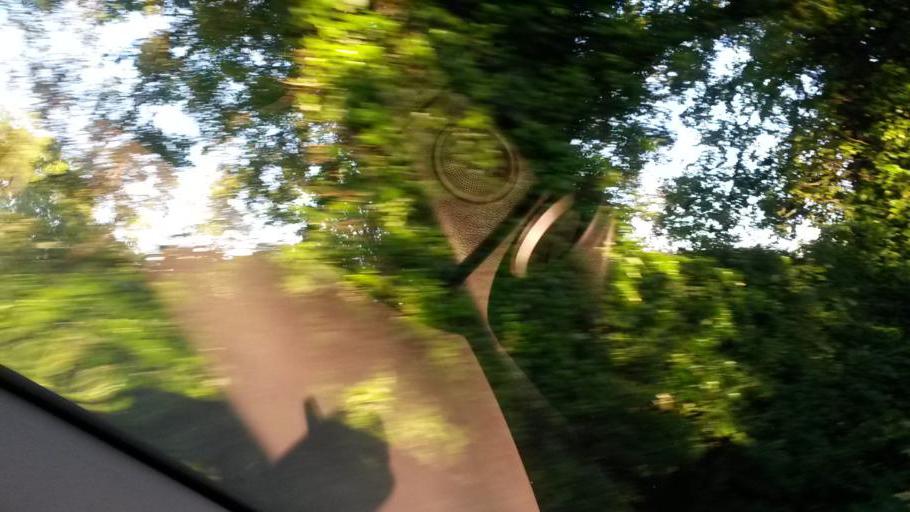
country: IE
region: Leinster
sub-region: An Mhi
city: Ashbourne
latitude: 53.4795
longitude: -6.3162
